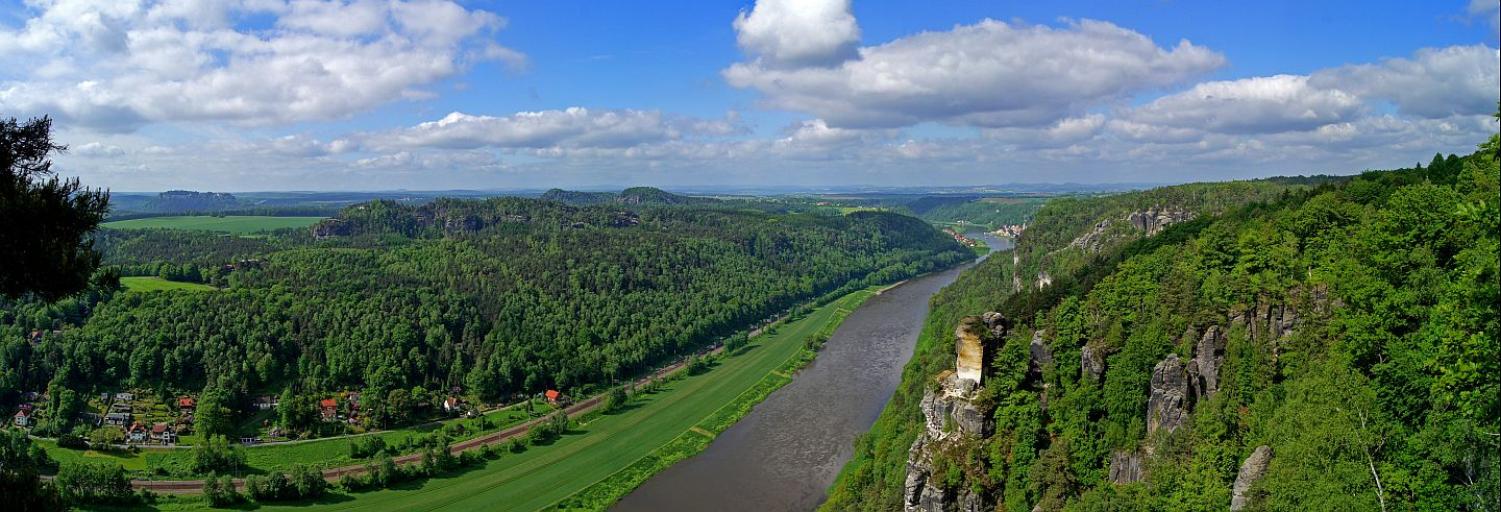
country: DE
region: Saxony
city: Stadt Wehlen
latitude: 50.9622
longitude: 14.0714
